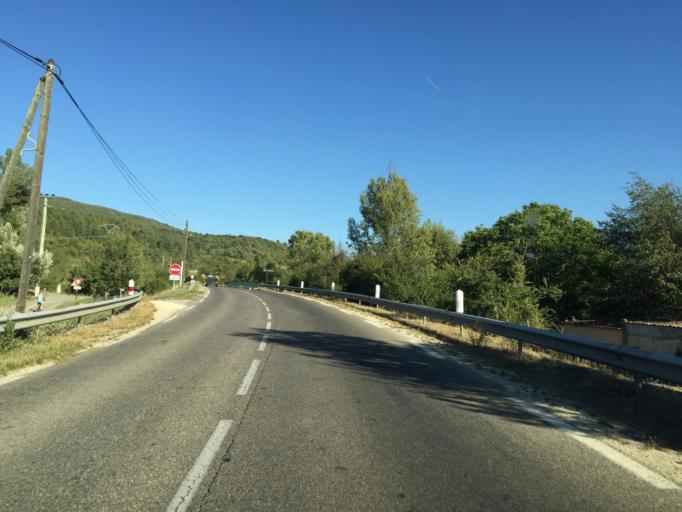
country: FR
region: Provence-Alpes-Cote d'Azur
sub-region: Departement du Vaucluse
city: Saignon
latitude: 43.8668
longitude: 5.4581
